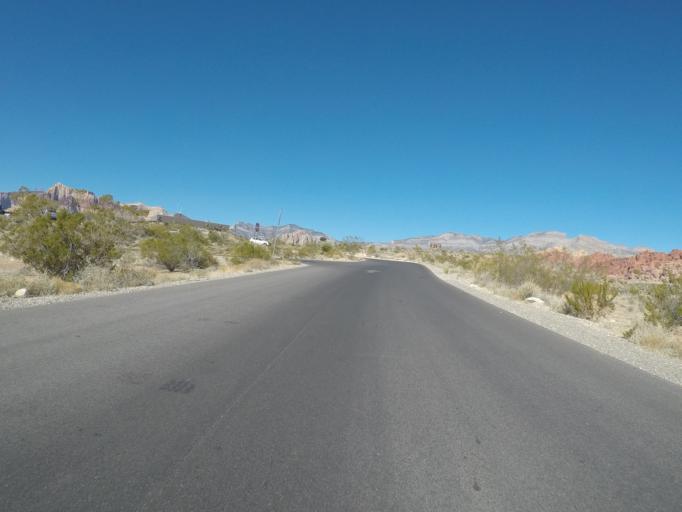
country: US
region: Nevada
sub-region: Clark County
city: Summerlin South
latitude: 36.1354
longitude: -115.4256
